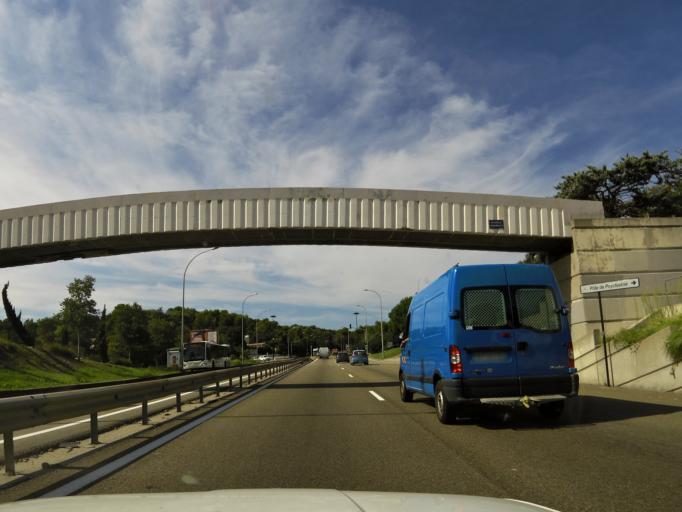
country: FR
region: Languedoc-Roussillon
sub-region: Departement du Gard
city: Nimes
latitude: 43.8294
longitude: 4.3238
